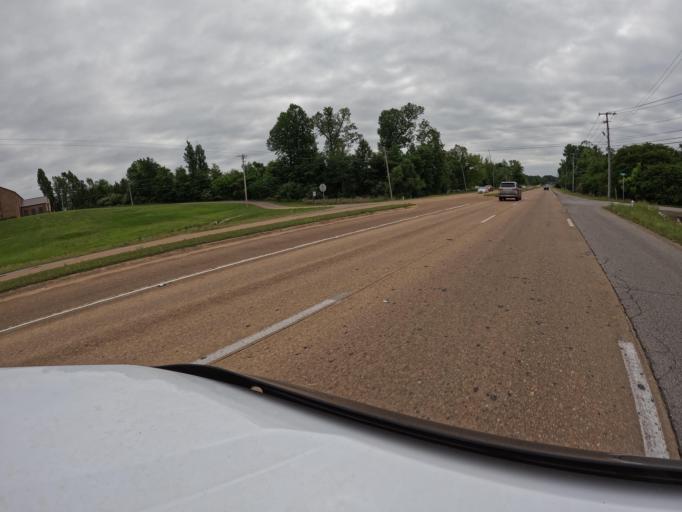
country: US
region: Mississippi
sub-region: Lee County
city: Tupelo
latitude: 34.2771
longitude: -88.7231
